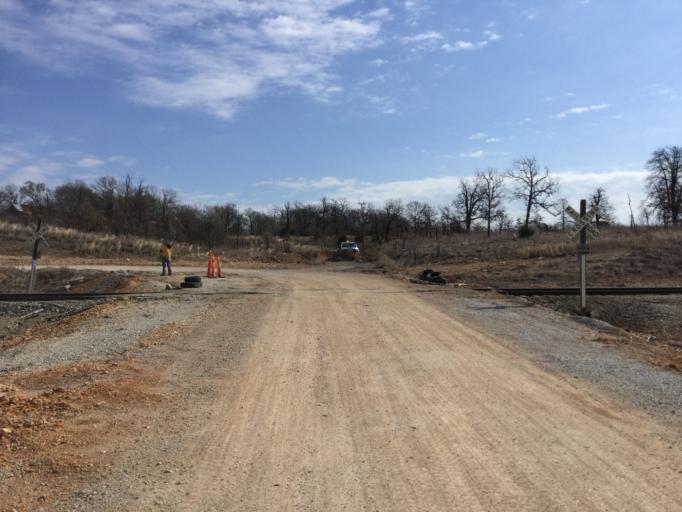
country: US
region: Kansas
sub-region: Cherokee County
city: Galena
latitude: 37.0803
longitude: -94.6276
